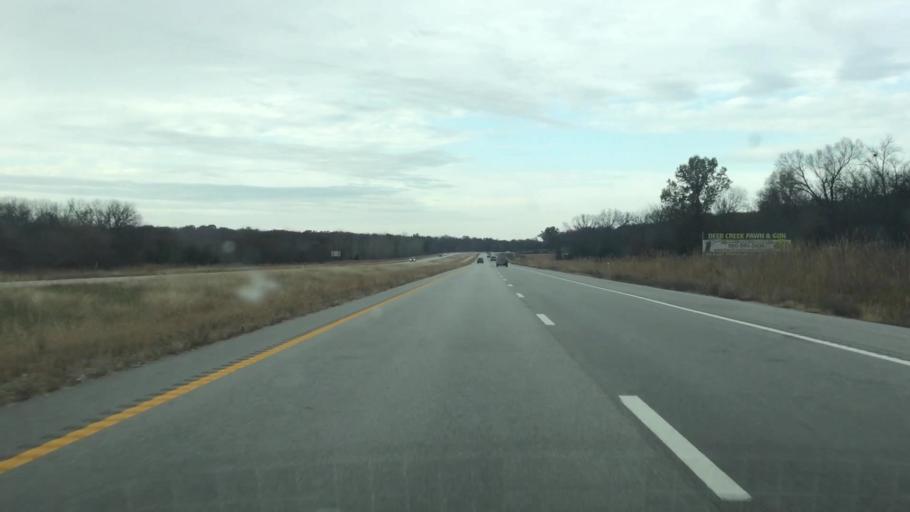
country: US
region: Missouri
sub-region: Henry County
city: Clinton
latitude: 38.2076
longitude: -93.7543
